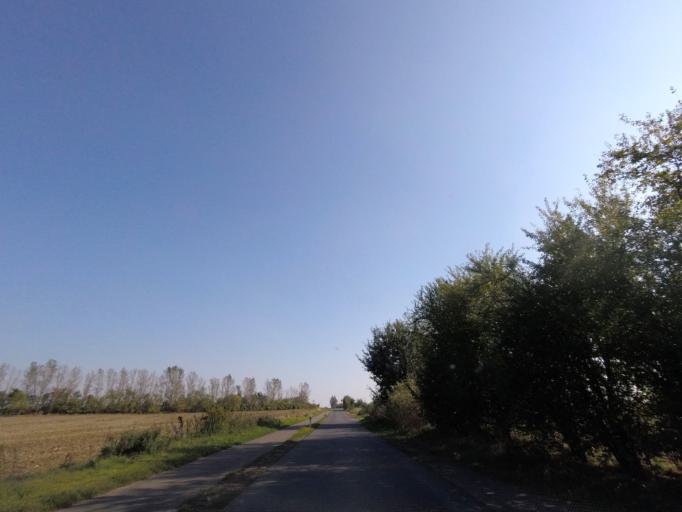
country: DE
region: Brandenburg
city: Niedergorsdorf
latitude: 51.9502
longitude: 12.9909
